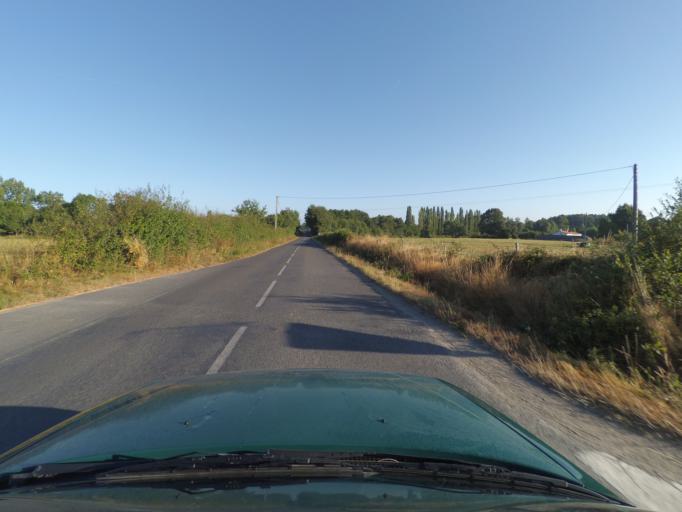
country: FR
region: Pays de la Loire
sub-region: Departement de la Loire-Atlantique
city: Montbert
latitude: 47.0497
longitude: -1.4824
